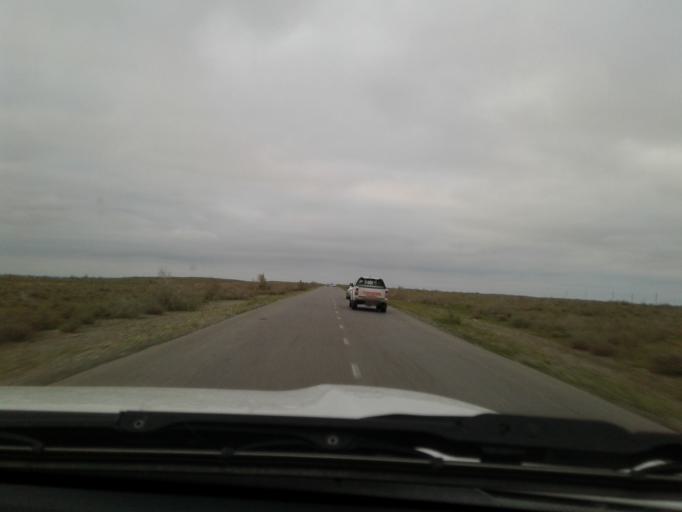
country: TM
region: Lebap
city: Turkmenabat
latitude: 39.0571
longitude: 63.7479
